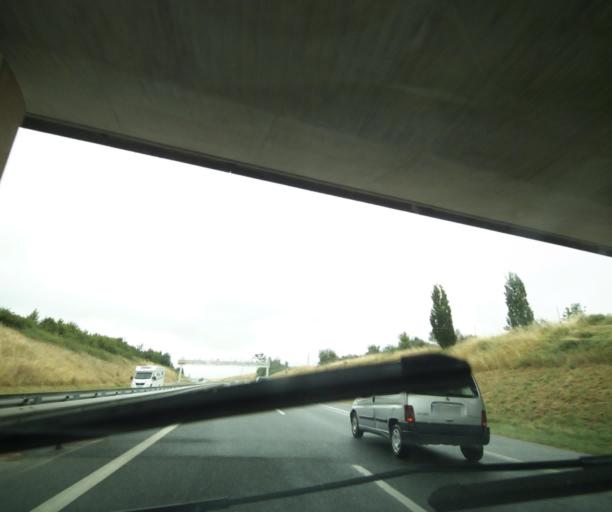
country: FR
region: Midi-Pyrenees
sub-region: Departement de l'Aveyron
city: Luc-la-Primaube
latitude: 44.3147
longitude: 2.5449
